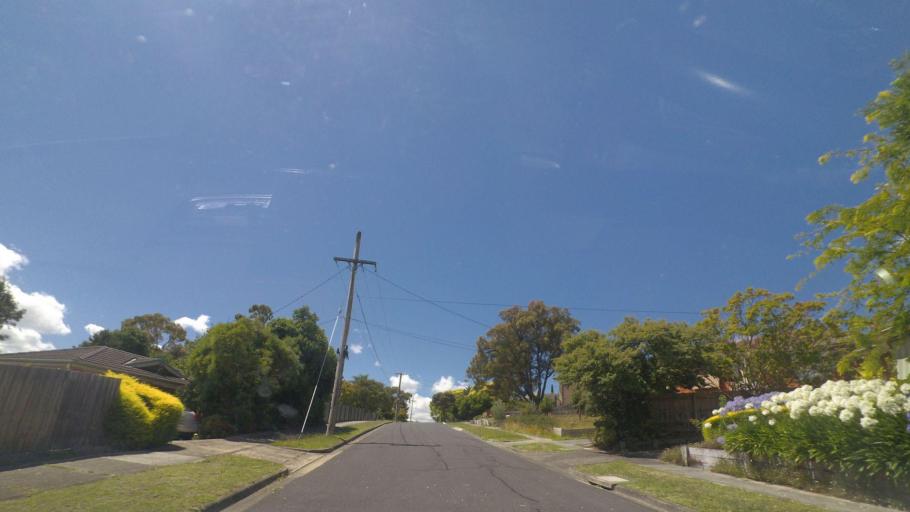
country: AU
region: Victoria
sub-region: Yarra Ranges
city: Kilsyth
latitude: -37.7912
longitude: 145.3217
